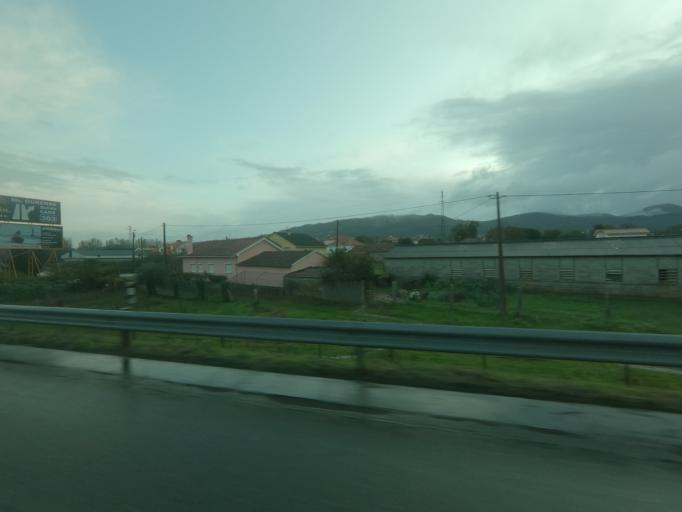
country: PT
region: Viana do Castelo
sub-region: Valenca
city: Valenza
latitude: 42.0074
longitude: -8.6469
